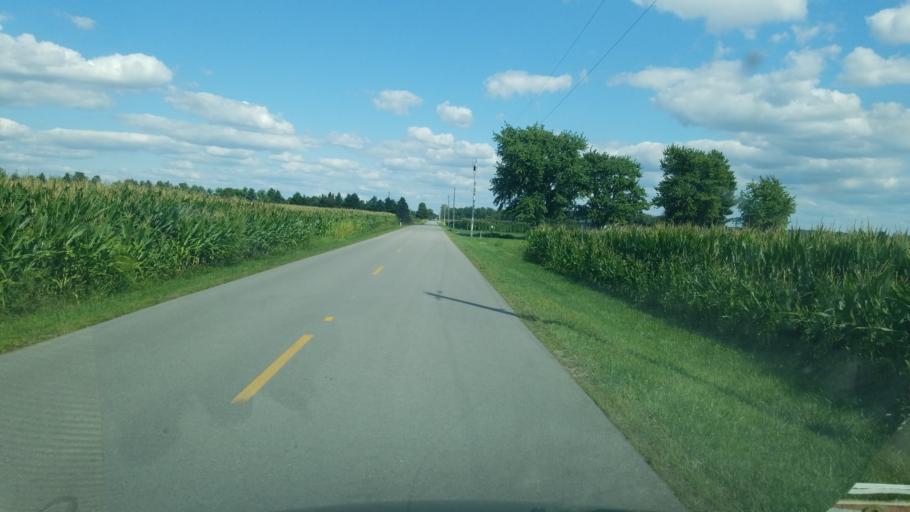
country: US
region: Ohio
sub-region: Logan County
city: Lakeview
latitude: 40.5134
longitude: -83.9533
